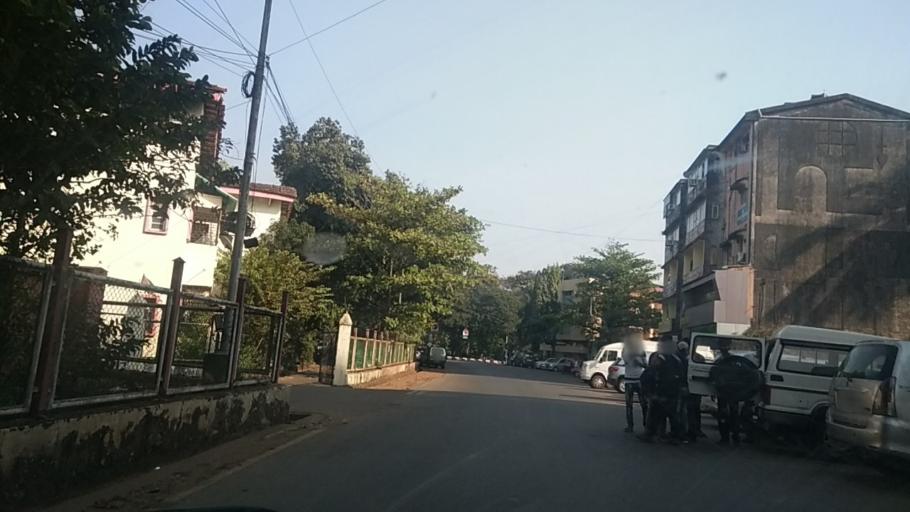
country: IN
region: Goa
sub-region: North Goa
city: Panaji
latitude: 15.4983
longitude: 73.8351
